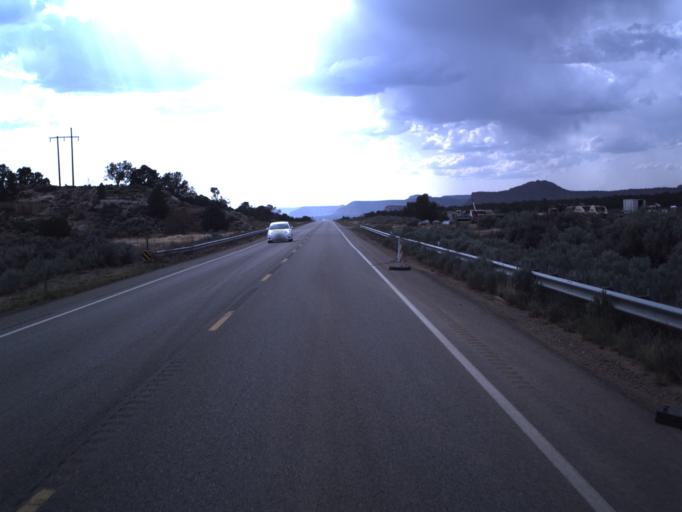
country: US
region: Utah
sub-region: Kane County
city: Kanab
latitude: 37.0404
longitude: -112.2497
